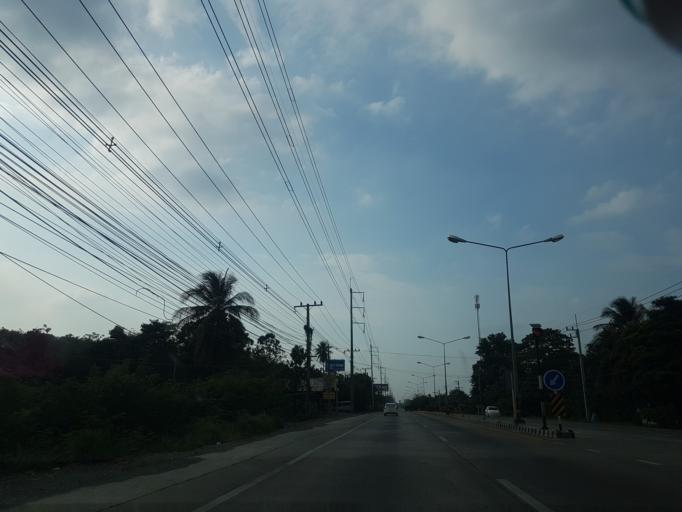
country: TH
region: Sara Buri
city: Nong Don
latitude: 14.7611
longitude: 100.7225
